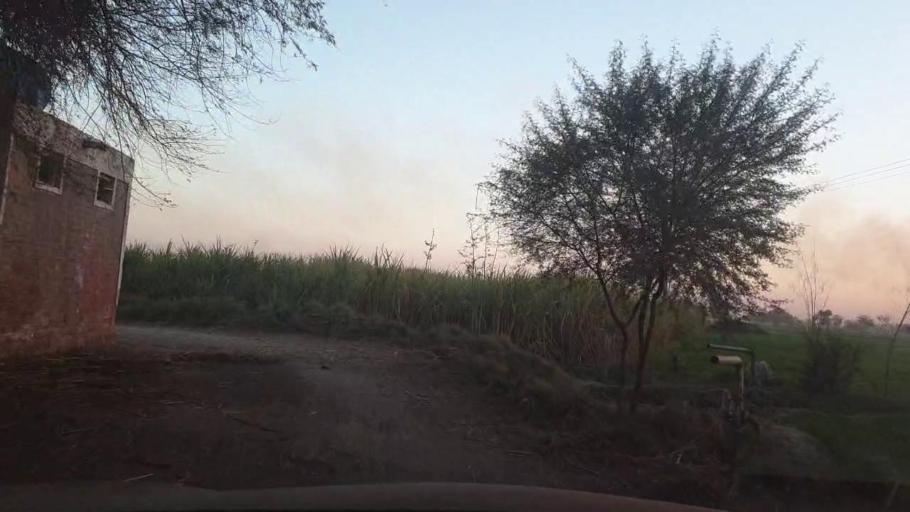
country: PK
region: Sindh
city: Ghotki
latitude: 28.0569
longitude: 69.3589
